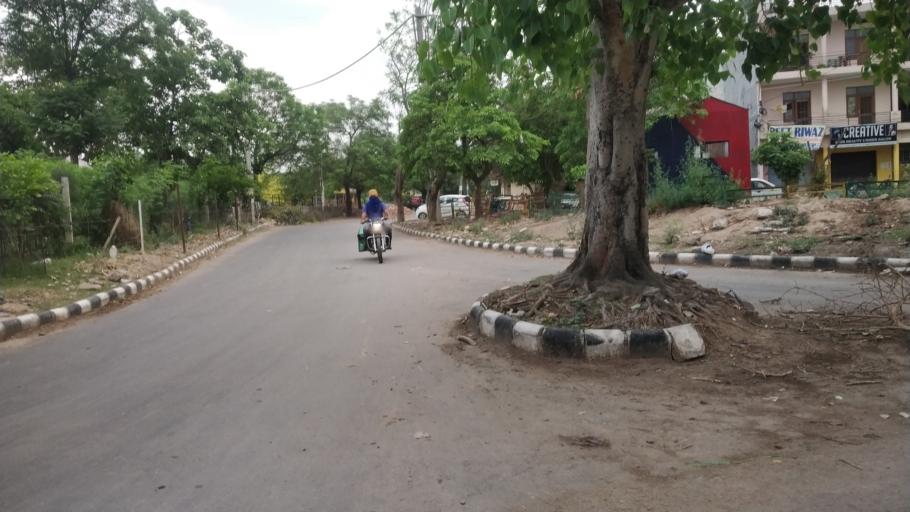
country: IN
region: Punjab
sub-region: Ajitgarh
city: Mohali
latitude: 30.7025
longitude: 76.7142
